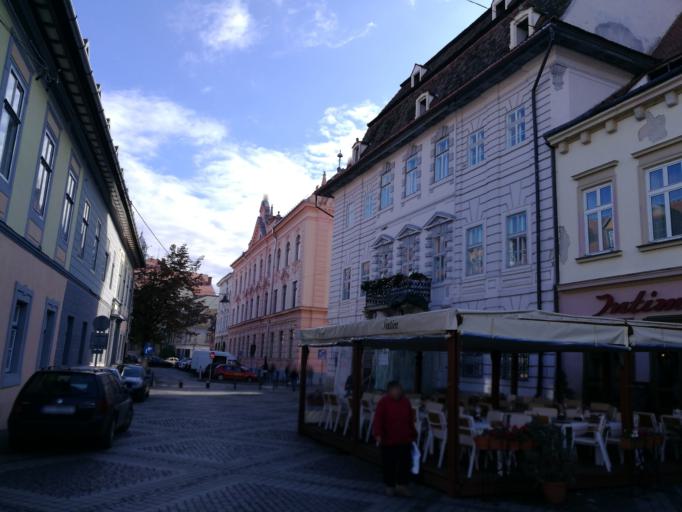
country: RO
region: Sibiu
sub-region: Municipiul Sibiu
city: Sibiu
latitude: 45.7966
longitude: 24.1526
